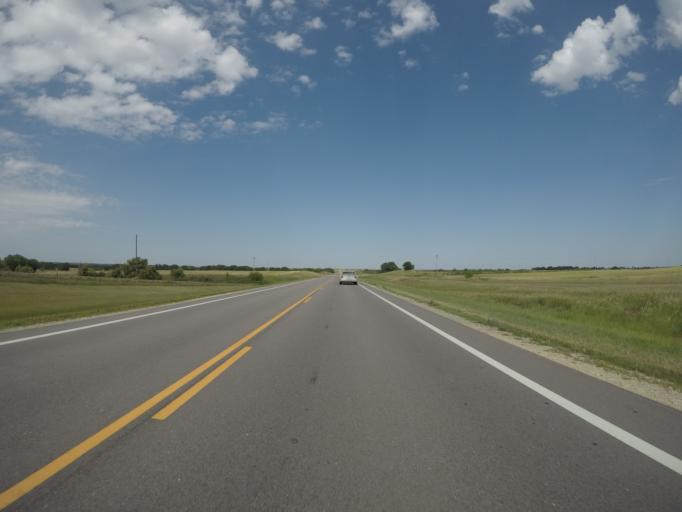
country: US
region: Kansas
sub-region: Clay County
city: Clay Center
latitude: 39.3789
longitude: -97.2925
